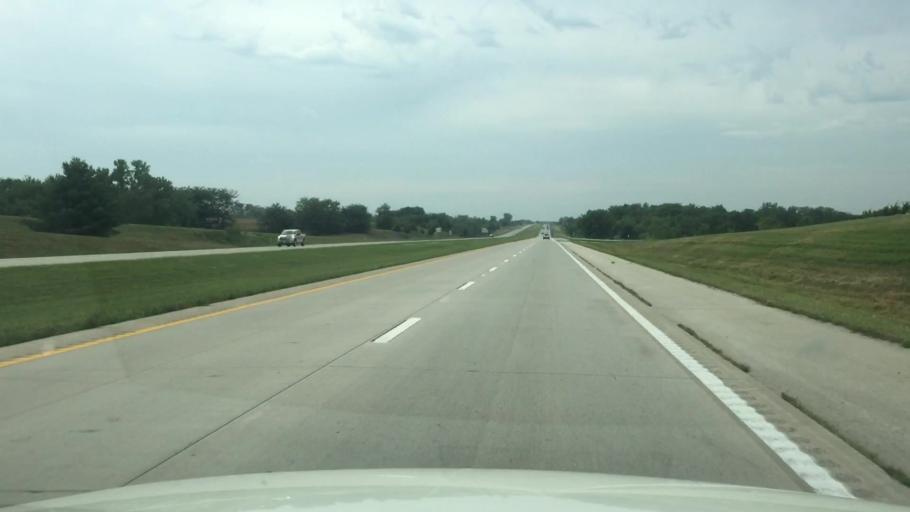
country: US
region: Missouri
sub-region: Daviess County
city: Gallatin
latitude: 39.9447
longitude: -94.1175
